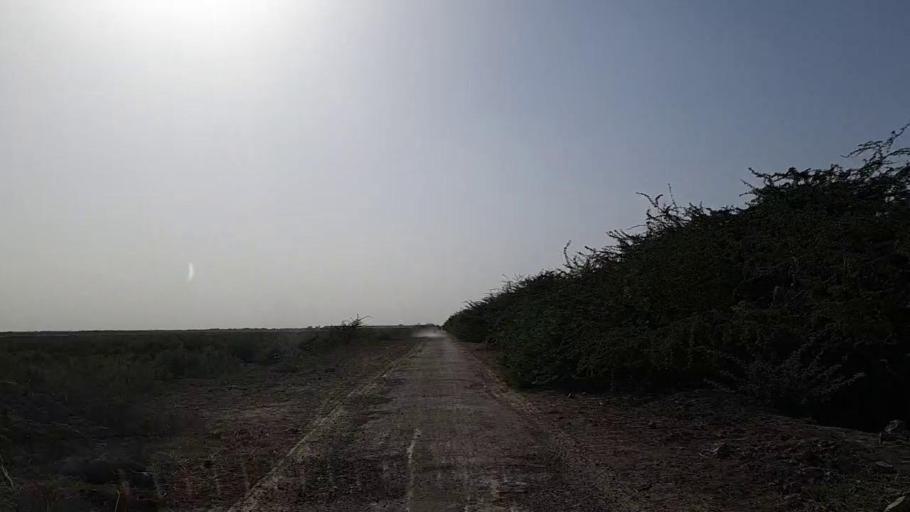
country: PK
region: Sindh
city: Jati
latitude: 24.2819
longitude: 68.2390
